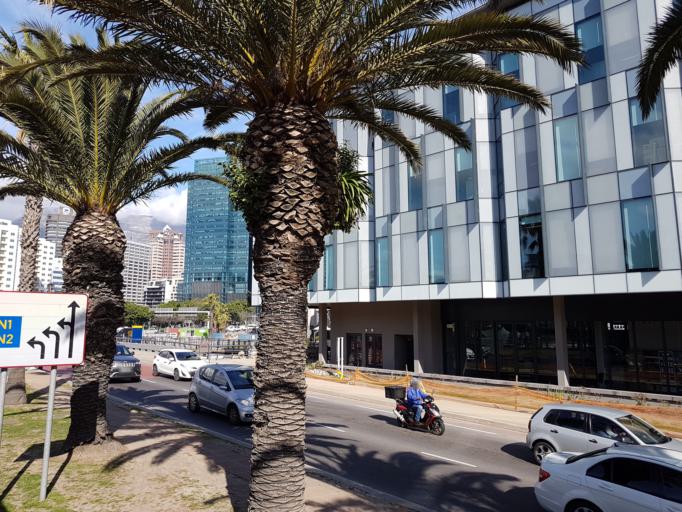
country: ZA
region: Western Cape
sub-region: City of Cape Town
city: Cape Town
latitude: -33.9131
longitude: 18.4232
